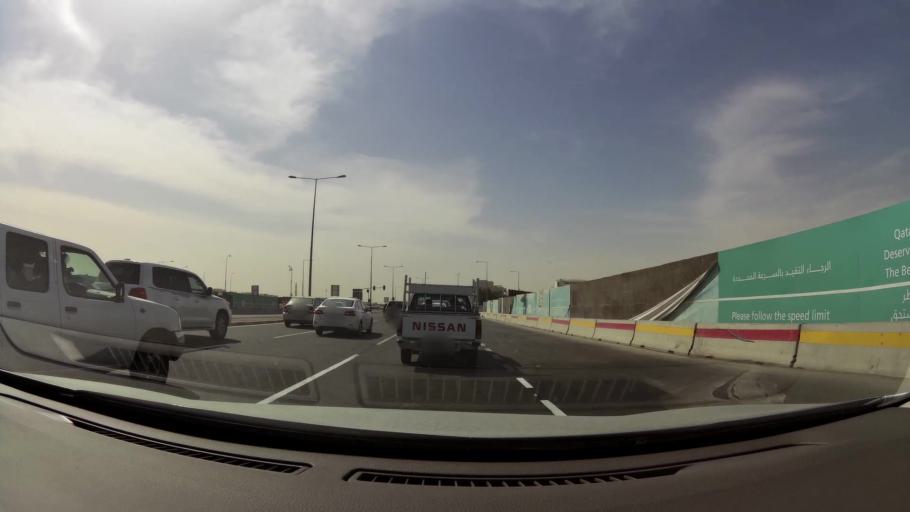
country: QA
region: Baladiyat ar Rayyan
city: Ar Rayyan
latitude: 25.3064
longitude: 51.4134
